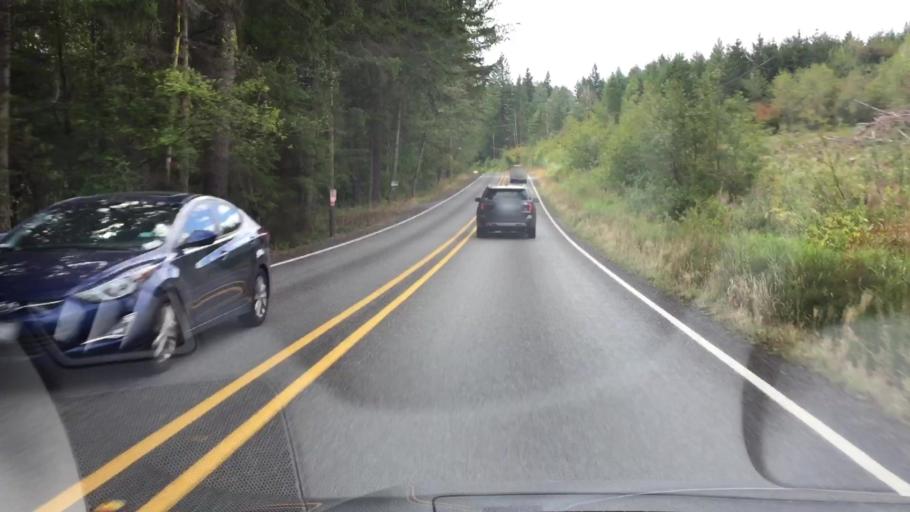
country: US
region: Washington
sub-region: Pierce County
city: Eatonville
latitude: 46.8222
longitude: -122.2625
